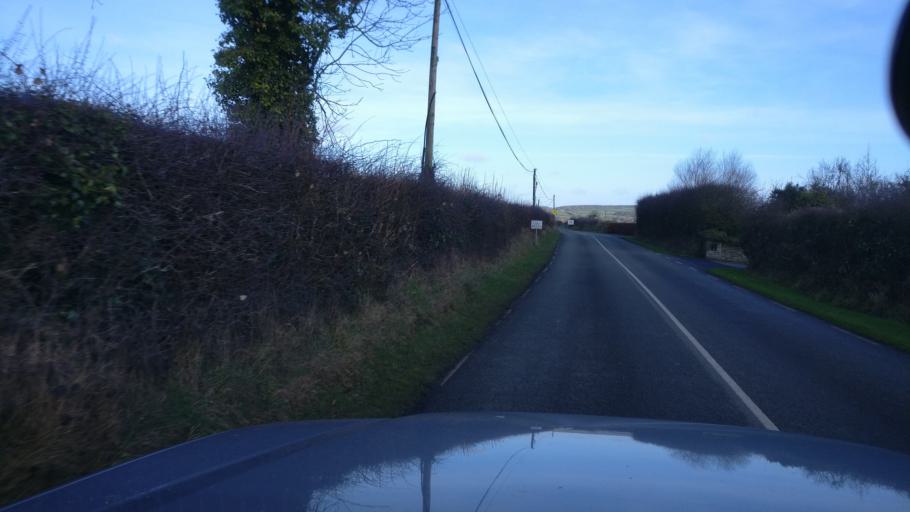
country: IE
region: Leinster
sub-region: Kilkenny
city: Castlecomer
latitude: 52.8553
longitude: -7.1709
